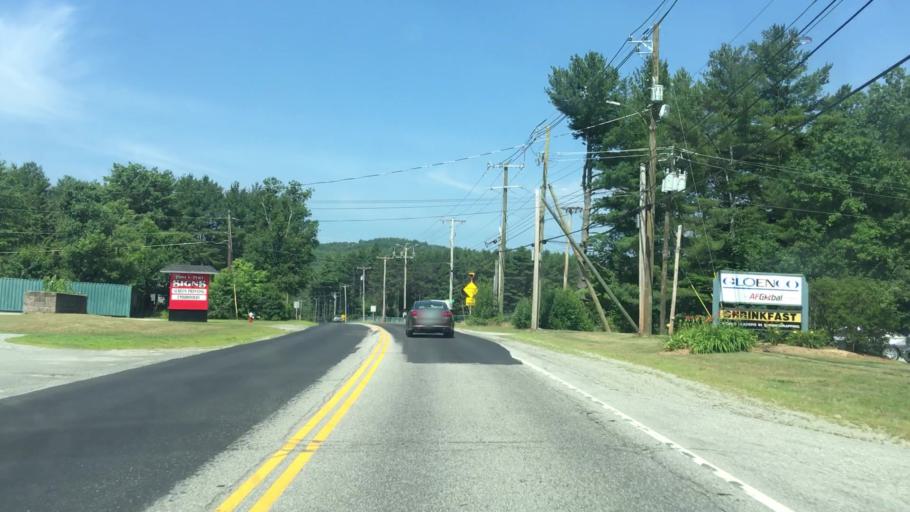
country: US
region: New Hampshire
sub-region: Sullivan County
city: Newport
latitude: 43.3796
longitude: -72.1443
